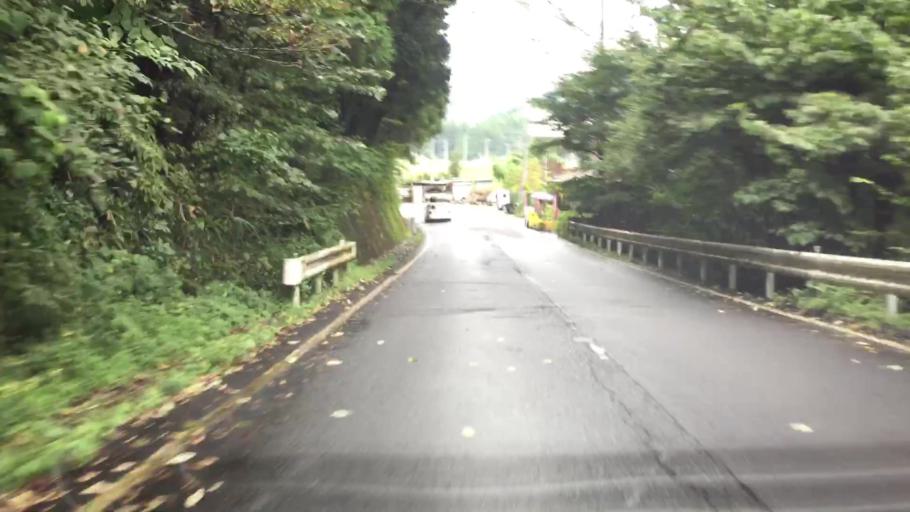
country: JP
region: Tochigi
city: Imaichi
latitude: 36.7620
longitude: 139.6799
